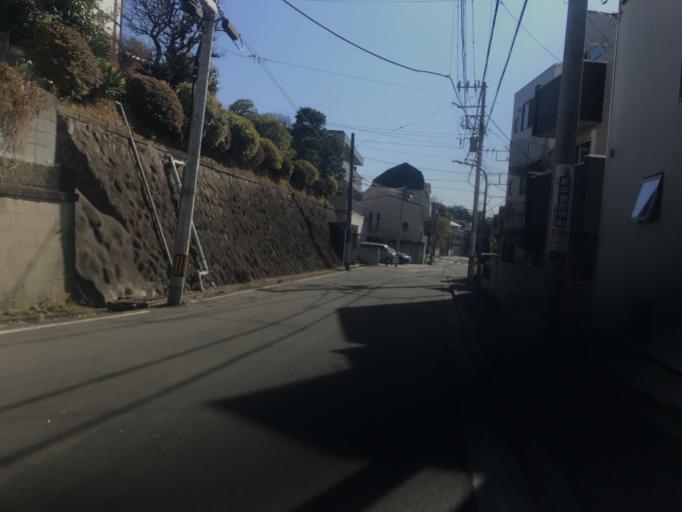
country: JP
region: Kanagawa
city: Yokohama
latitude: 35.4876
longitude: 139.6286
